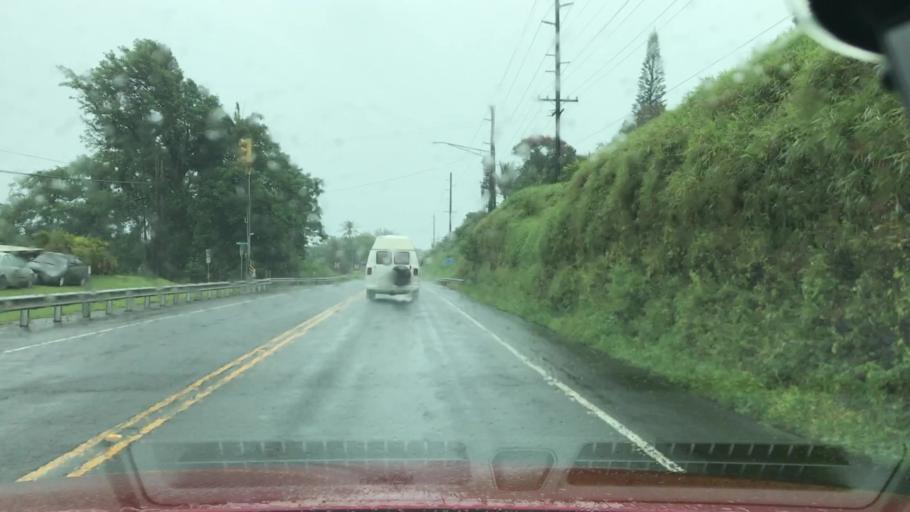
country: US
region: Hawaii
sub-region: Hawaii County
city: Pepeekeo
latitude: 19.9854
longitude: -155.2379
